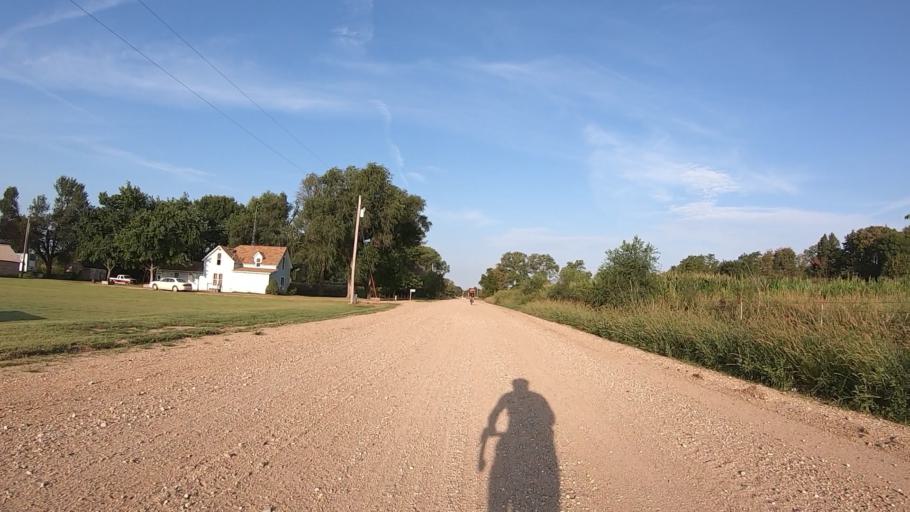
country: US
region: Kansas
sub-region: Marshall County
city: Blue Rapids
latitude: 39.7263
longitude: -96.7916
